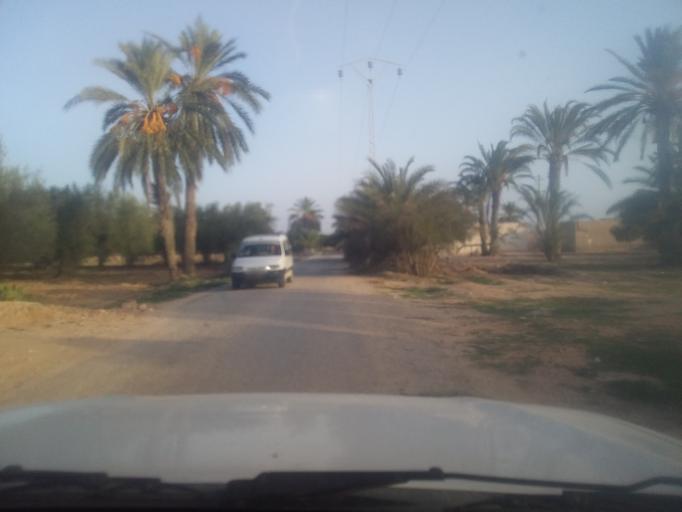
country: TN
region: Qabis
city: Gabes
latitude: 33.6195
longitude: 10.2981
